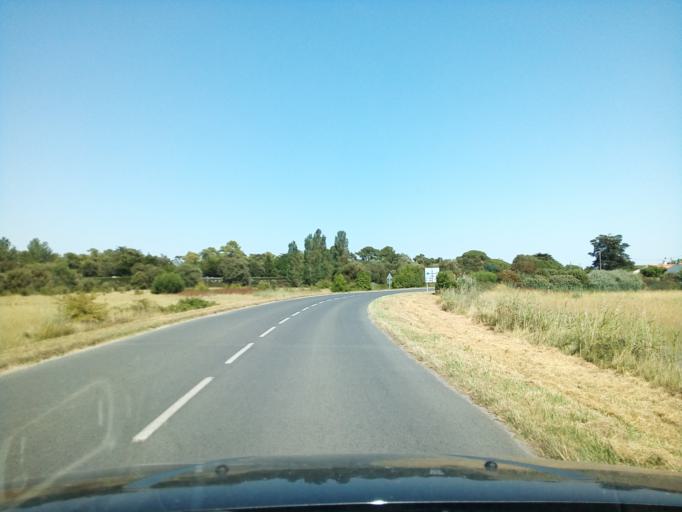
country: FR
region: Poitou-Charentes
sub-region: Departement de la Charente-Maritime
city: Boyard-Ville
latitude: 45.9672
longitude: -1.2496
